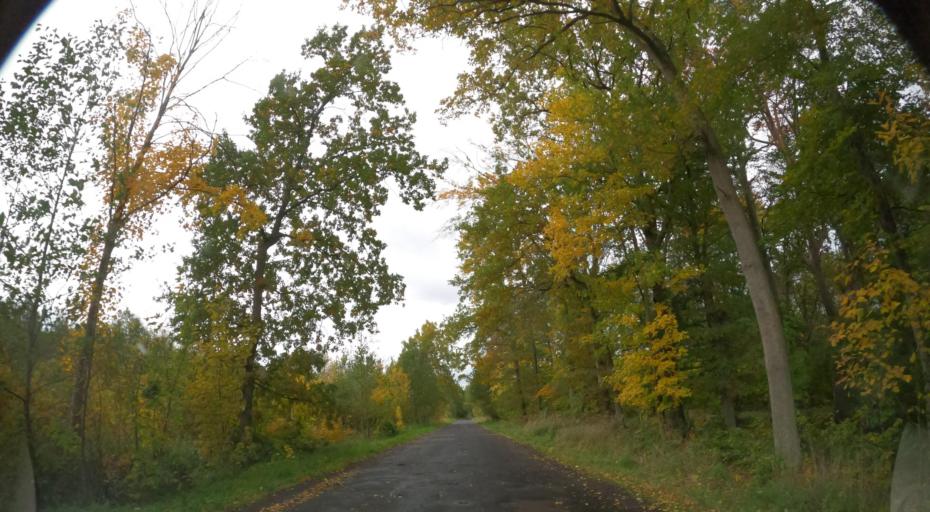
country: PL
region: West Pomeranian Voivodeship
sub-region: Powiat goleniowski
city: Stepnica
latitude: 53.6633
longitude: 14.6636
